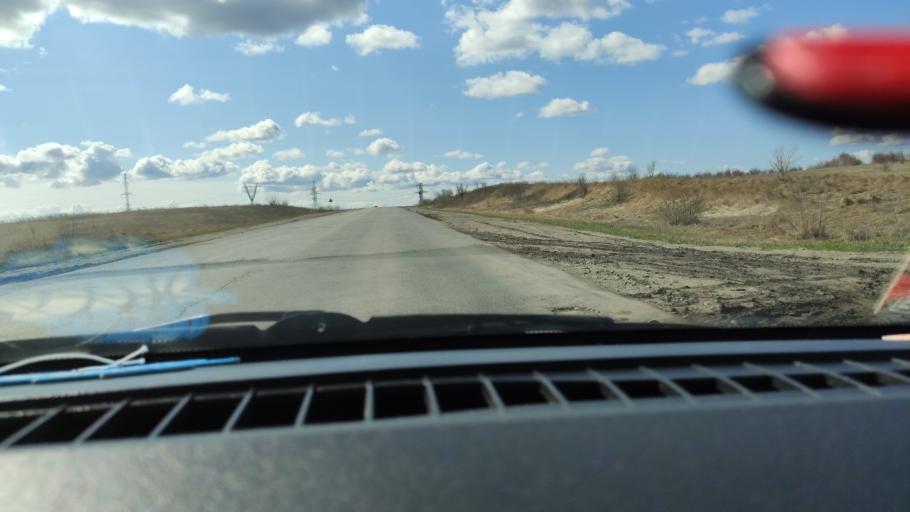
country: RU
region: Samara
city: Varlamovo
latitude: 53.0839
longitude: 48.3546
